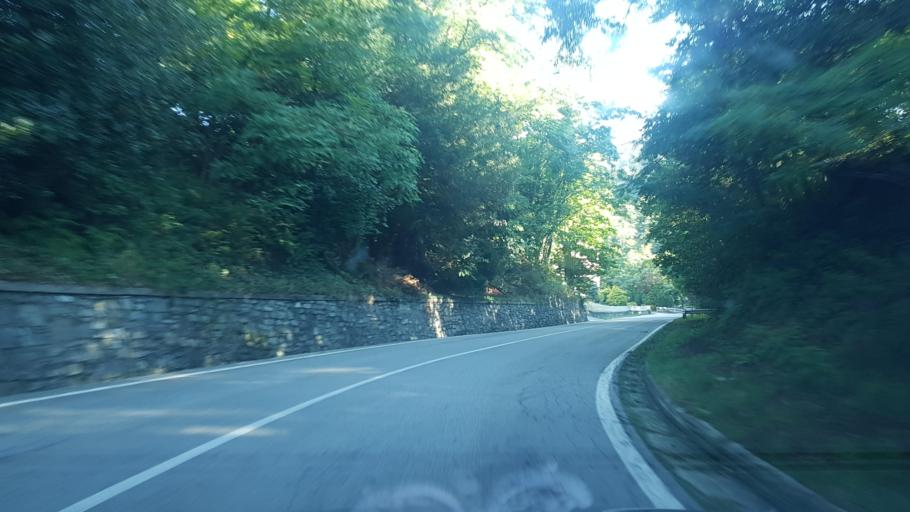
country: IT
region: Piedmont
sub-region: Provincia Verbano-Cusio-Ossola
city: Bee
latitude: 45.9730
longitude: 8.5829
